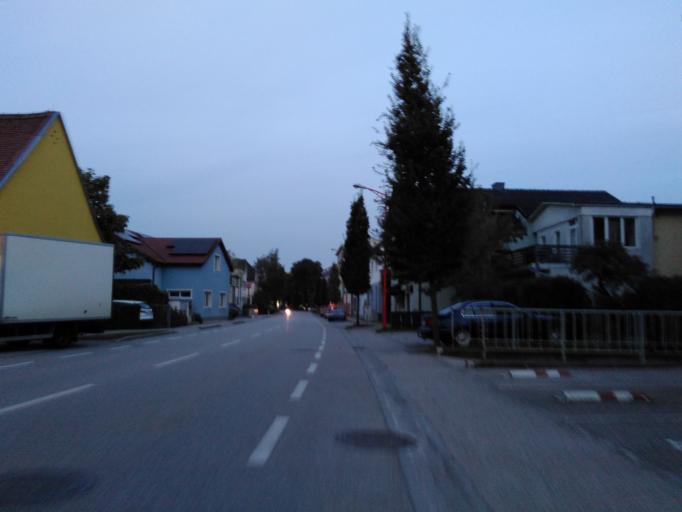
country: AT
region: Lower Austria
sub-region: Politischer Bezirk Amstetten
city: Sankt Valentin
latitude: 48.1725
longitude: 14.5172
